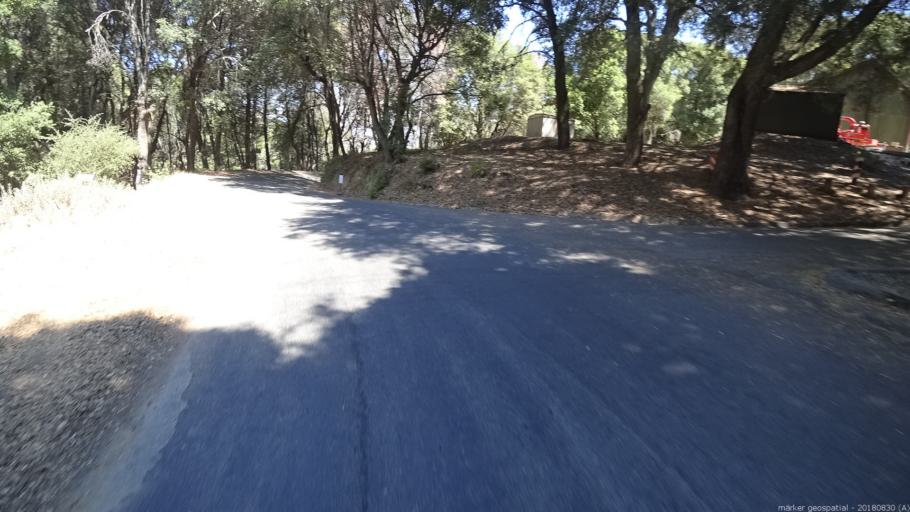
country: US
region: California
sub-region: Monterey County
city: Greenfield
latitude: 36.0089
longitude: -121.4500
